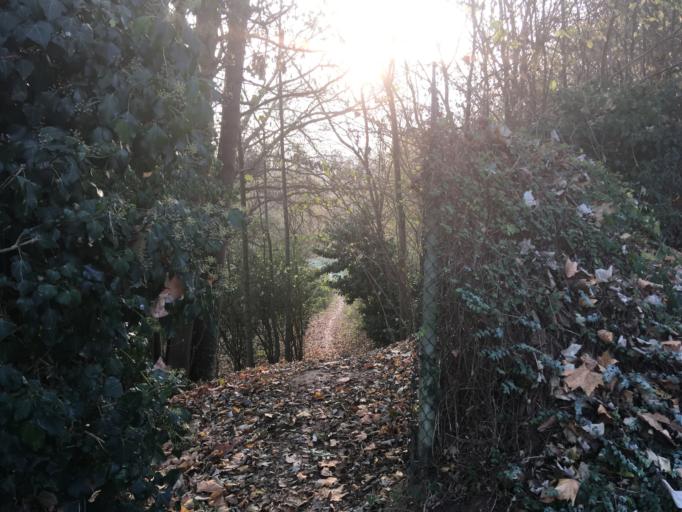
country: BE
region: Flanders
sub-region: Provincie Vlaams-Brabant
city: Beersel
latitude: 50.7279
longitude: 4.3079
